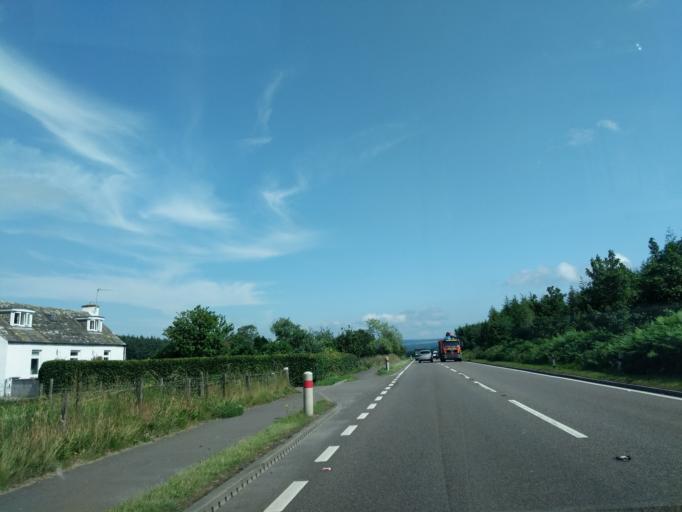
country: GB
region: Scotland
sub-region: Moray
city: Lhanbryd
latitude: 57.6274
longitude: -3.1642
